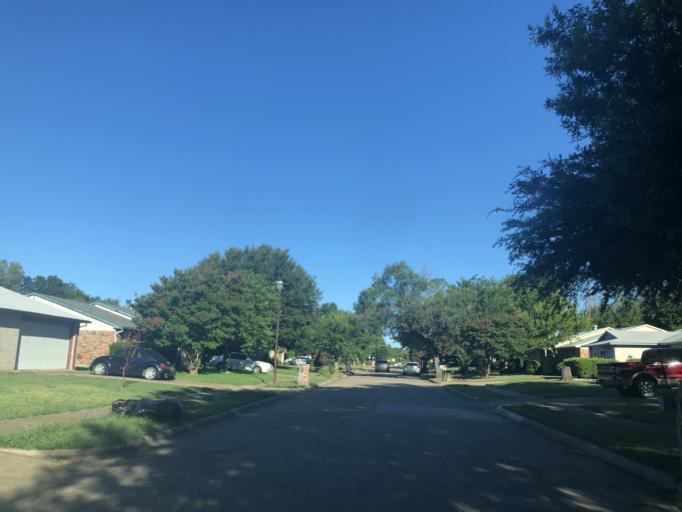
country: US
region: Texas
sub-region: Dallas County
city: Duncanville
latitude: 32.6443
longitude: -96.9509
